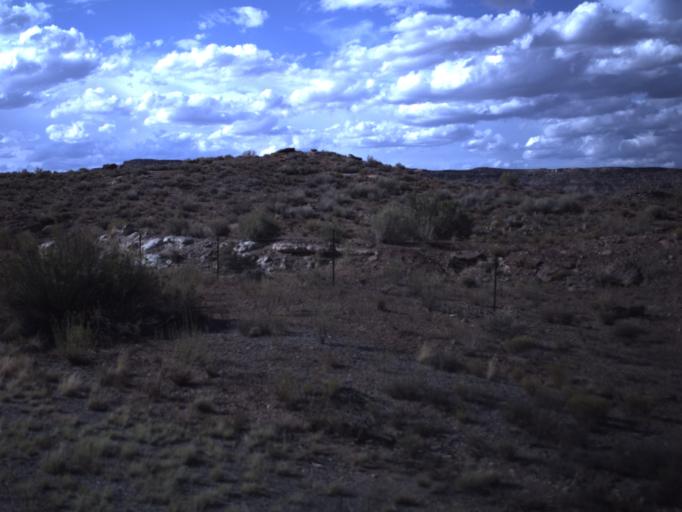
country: US
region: Utah
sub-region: San Juan County
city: Blanding
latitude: 37.3069
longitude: -109.2911
